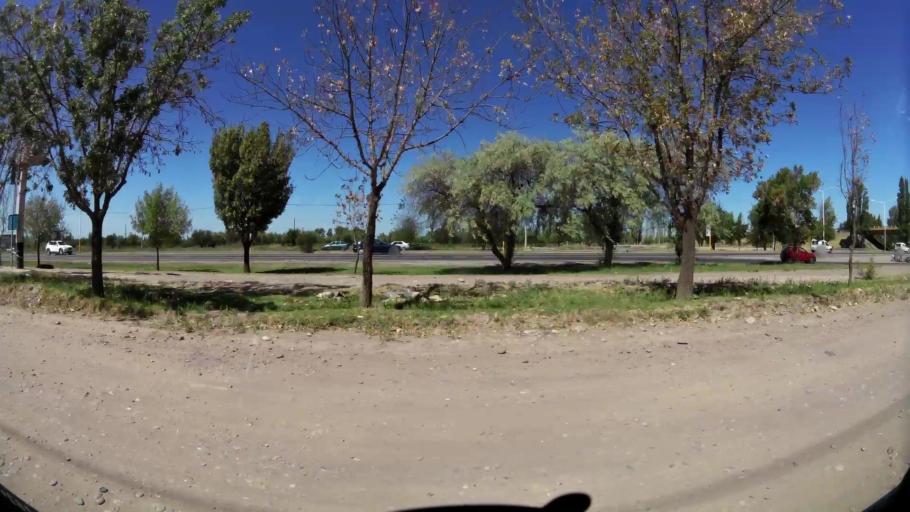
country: AR
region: Mendoza
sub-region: Departamento de Godoy Cruz
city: Godoy Cruz
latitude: -32.9832
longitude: -68.8496
